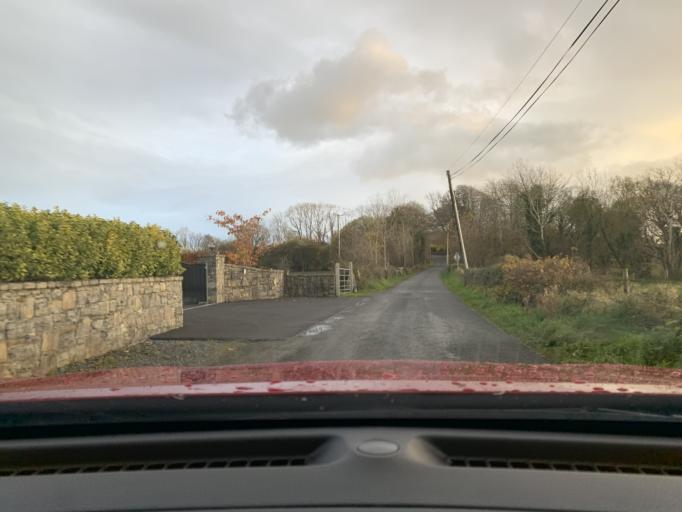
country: IE
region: Connaught
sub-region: Sligo
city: Sligo
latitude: 54.3027
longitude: -8.4924
